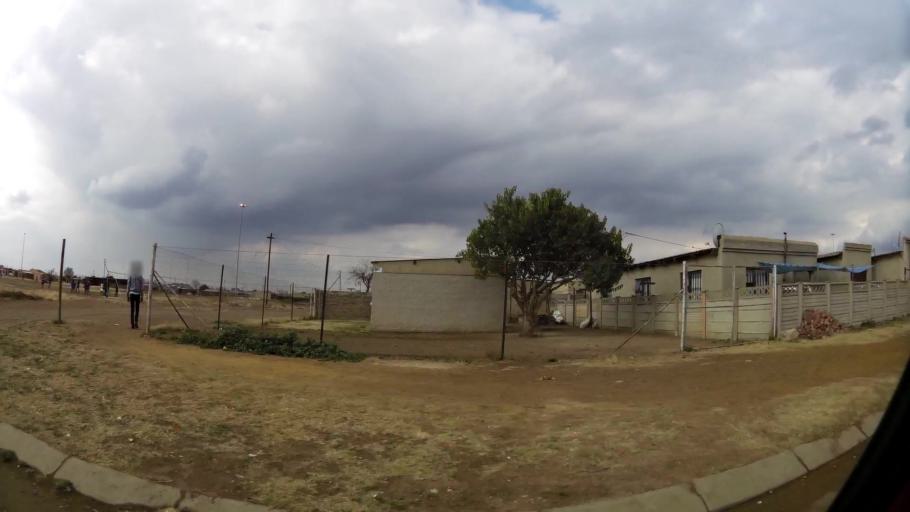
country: ZA
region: Gauteng
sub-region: Sedibeng District Municipality
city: Vanderbijlpark
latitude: -26.6876
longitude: 27.7801
